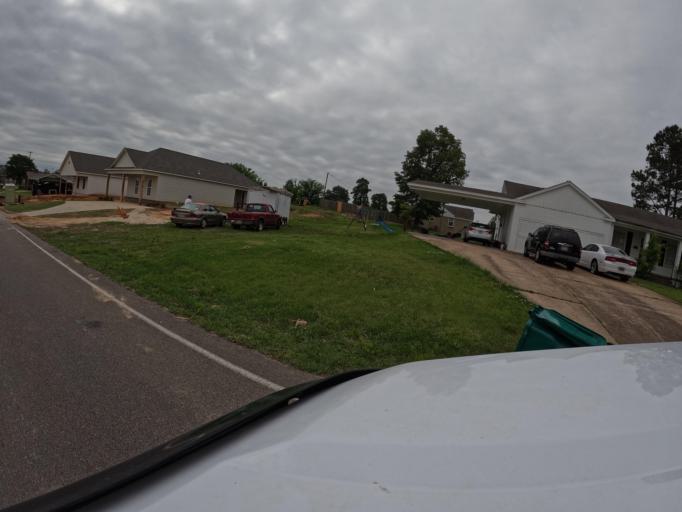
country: US
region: Mississippi
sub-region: Lee County
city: Tupelo
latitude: 34.2775
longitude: -88.7278
